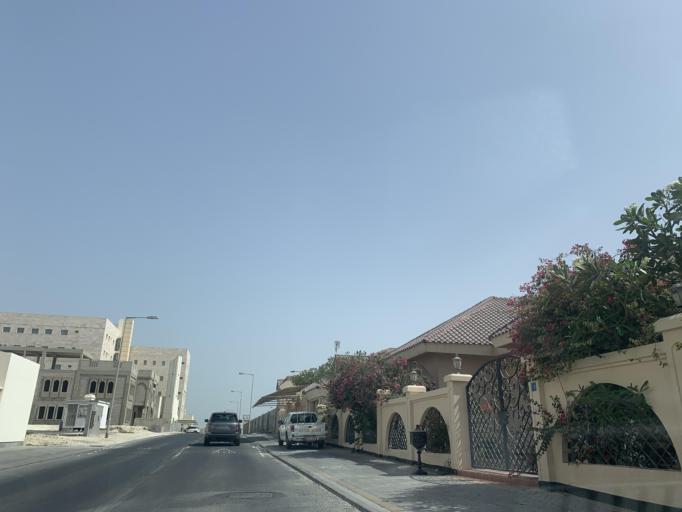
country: BH
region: Northern
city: Ar Rifa'
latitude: 26.1517
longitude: 50.5670
